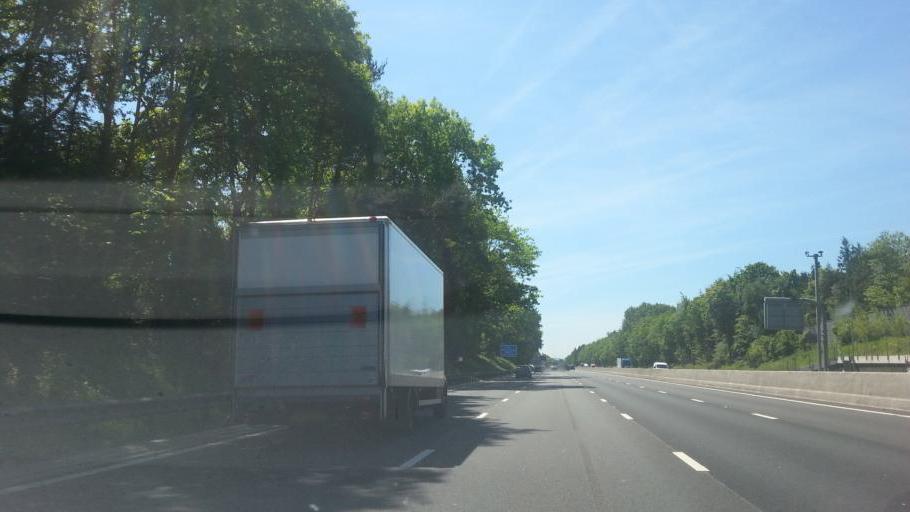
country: GB
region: England
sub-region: Surrey
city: Camberley
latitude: 51.3324
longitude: -0.7247
